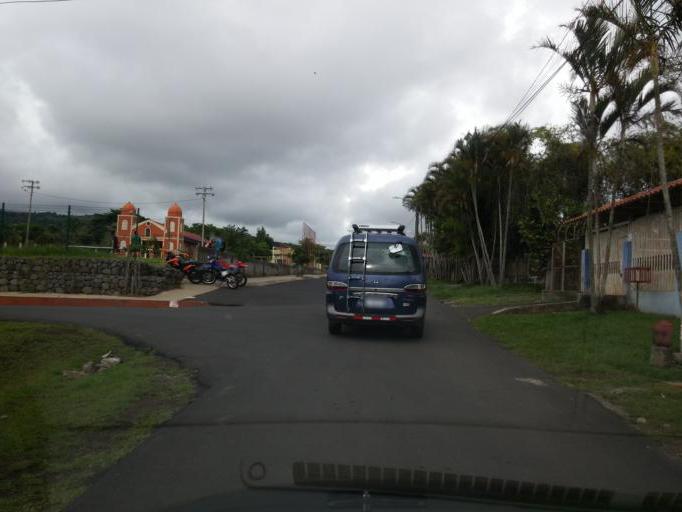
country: CR
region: Heredia
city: Santo Domingo
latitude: 10.0404
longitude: -84.1470
